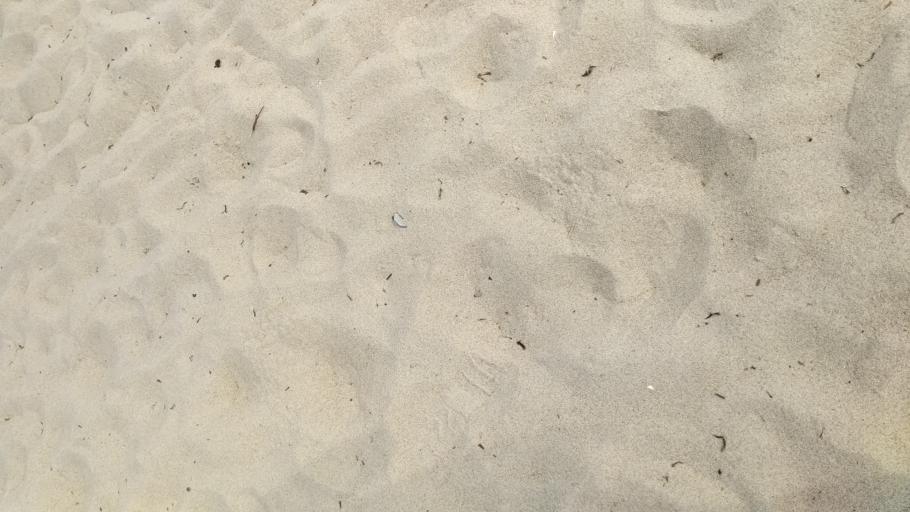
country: DK
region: Zealand
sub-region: Odsherred Kommune
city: Asnaes
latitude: 55.8472
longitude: 11.4935
